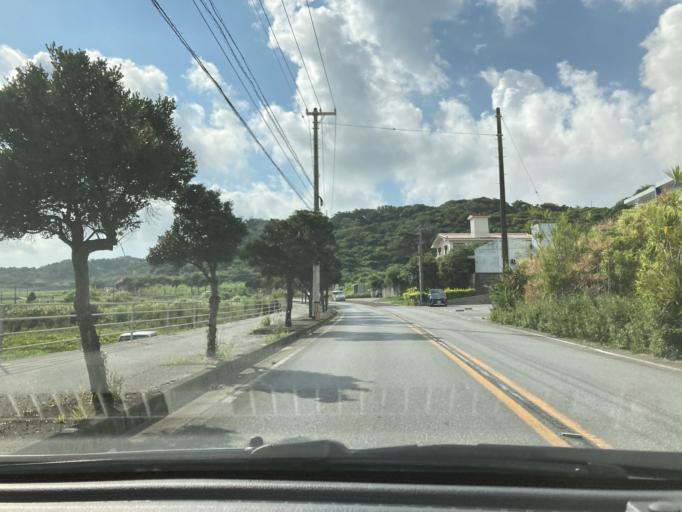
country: JP
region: Okinawa
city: Tomigusuku
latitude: 26.1506
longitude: 127.7528
